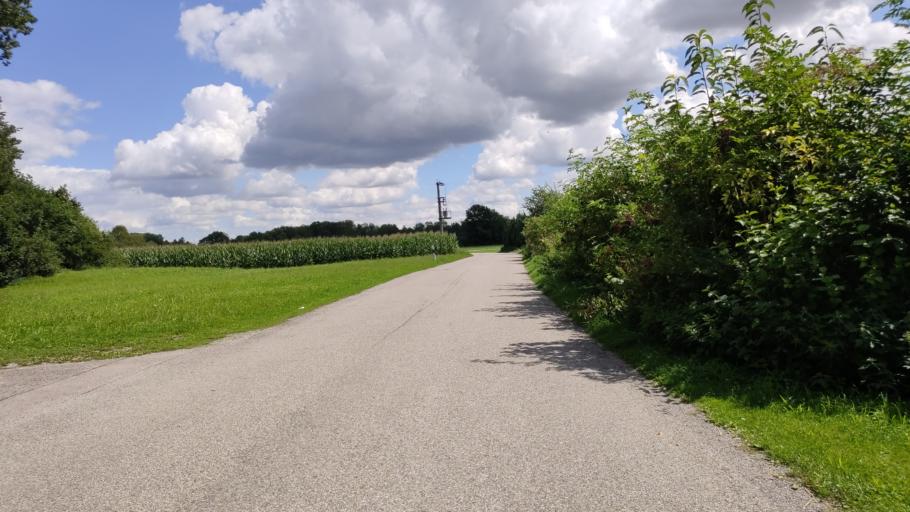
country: DE
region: Bavaria
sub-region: Swabia
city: Konigsbrunn
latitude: 48.2517
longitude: 10.9055
